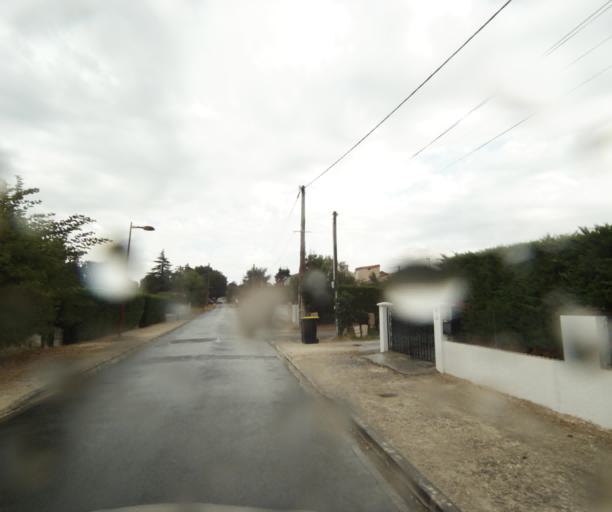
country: FR
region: Aquitaine
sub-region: Departement de la Gironde
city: Creon
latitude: 44.7678
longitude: -0.3514
